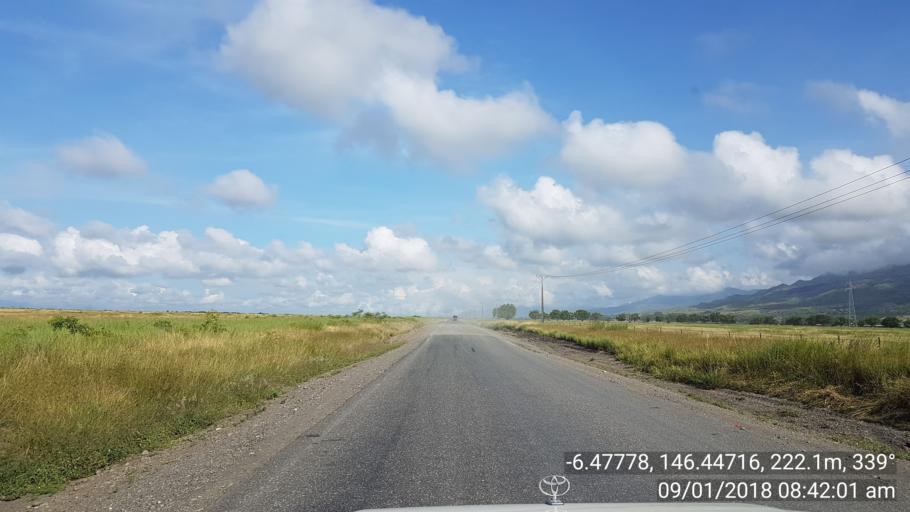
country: PG
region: Morobe
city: Lae
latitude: -6.4780
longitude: 146.4472
